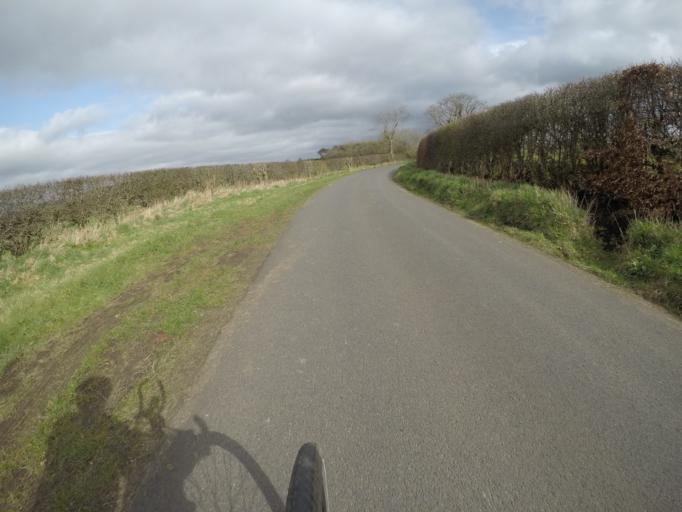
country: GB
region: Scotland
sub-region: North Ayrshire
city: Irvine
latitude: 55.6376
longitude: -4.6311
